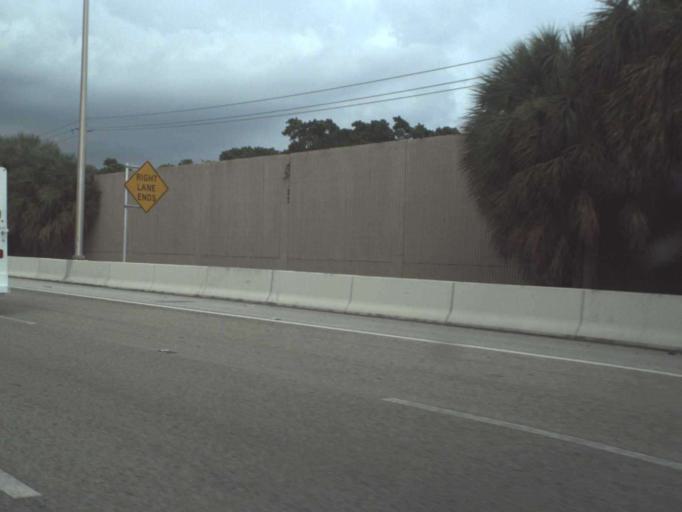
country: US
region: Florida
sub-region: Palm Beach County
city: West Palm Beach
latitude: 26.7103
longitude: -80.0787
